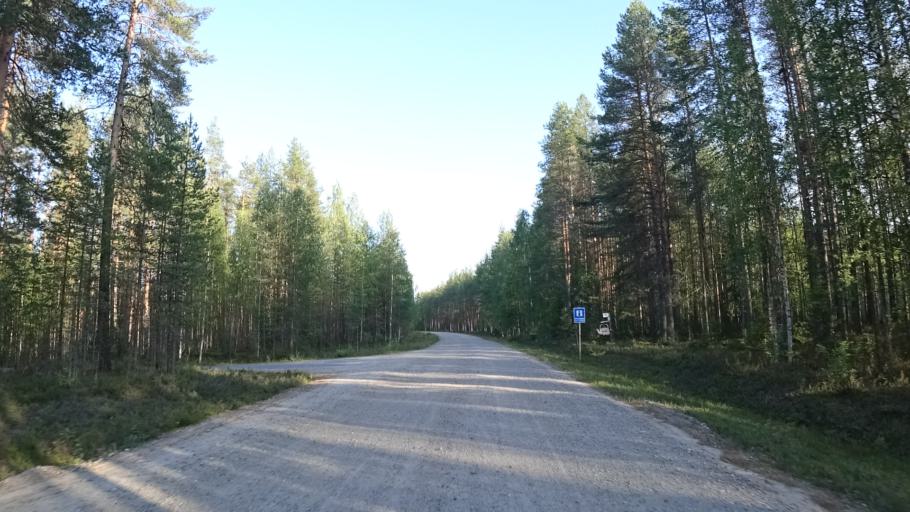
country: FI
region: North Karelia
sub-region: Joensuu
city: Ilomantsi
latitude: 63.1294
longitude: 30.7125
